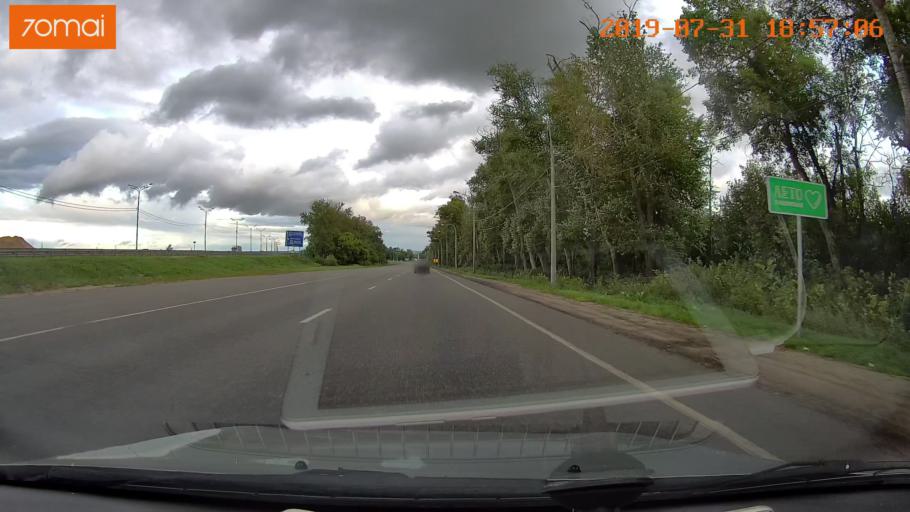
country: RU
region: Moskovskaya
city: Raduzhnyy
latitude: 55.1569
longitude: 38.6876
